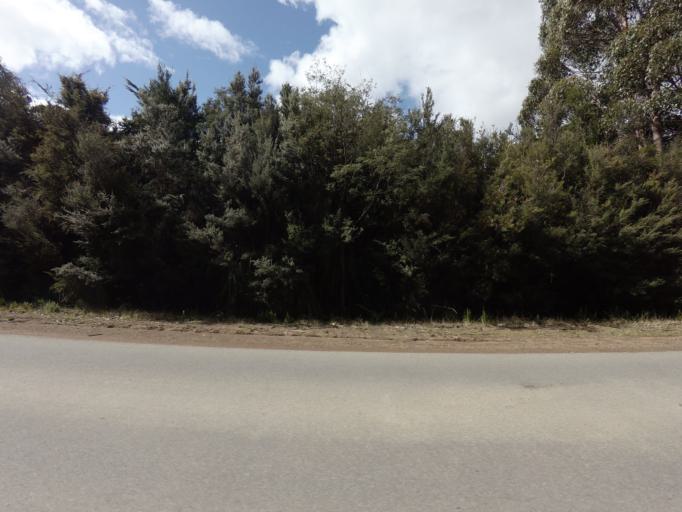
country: AU
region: Tasmania
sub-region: Huon Valley
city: Geeveston
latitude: -43.3545
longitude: 146.9578
